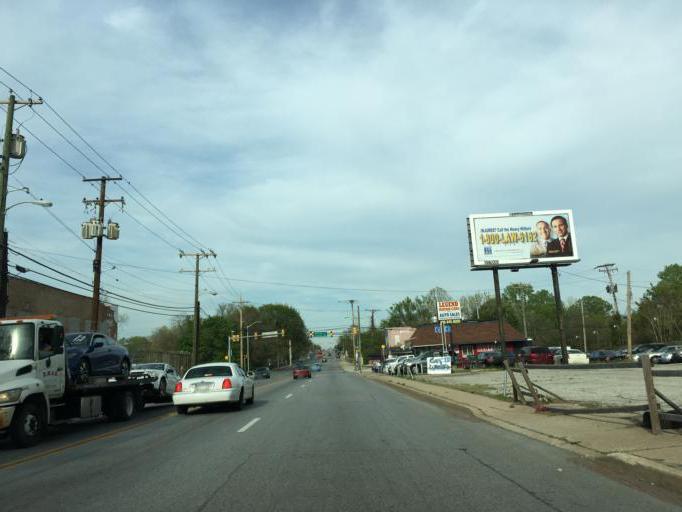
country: US
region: Maryland
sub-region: Baltimore County
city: Lansdowne
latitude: 39.2764
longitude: -76.6636
